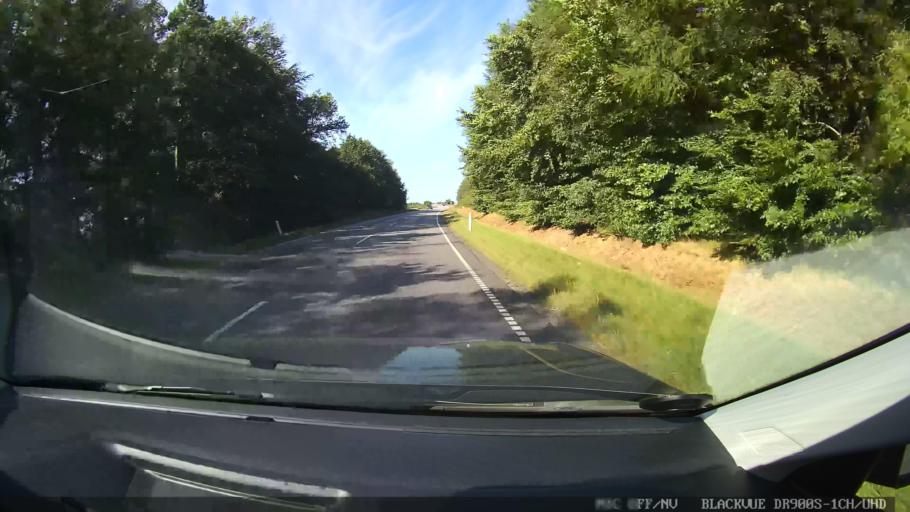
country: DK
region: North Denmark
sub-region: Mariagerfjord Kommune
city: Hobro
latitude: 56.6670
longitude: 9.7431
